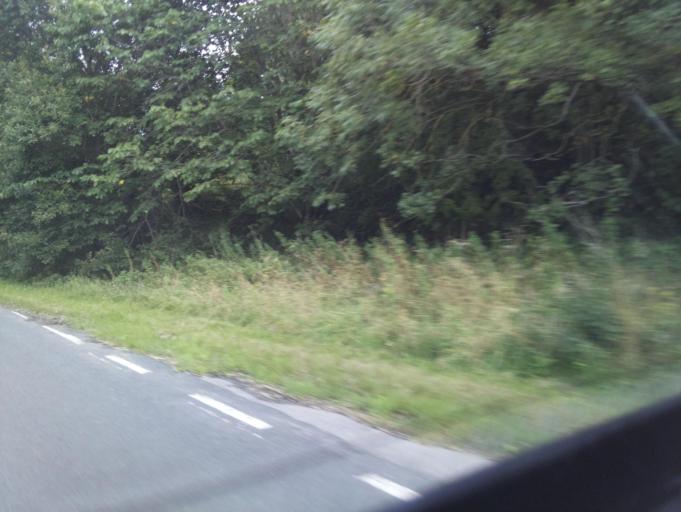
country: GB
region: England
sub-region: North Yorkshire
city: Leyburn
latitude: 54.3920
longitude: -1.8278
